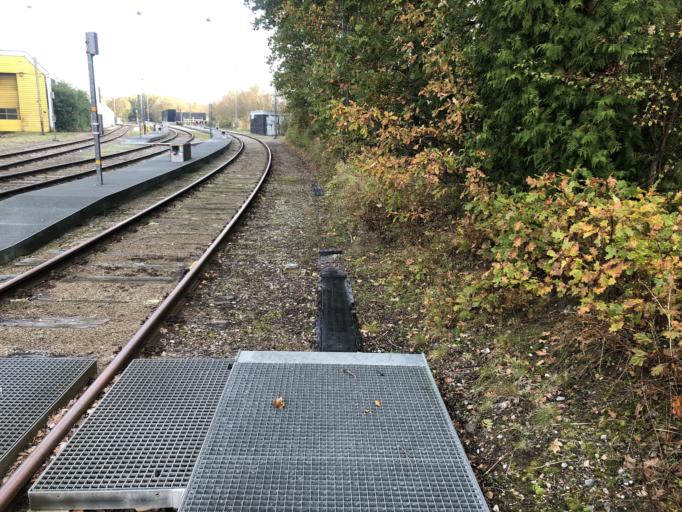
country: DK
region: Zealand
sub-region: Guldborgsund Kommune
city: Nykobing Falster
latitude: 54.7756
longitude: 11.8847
